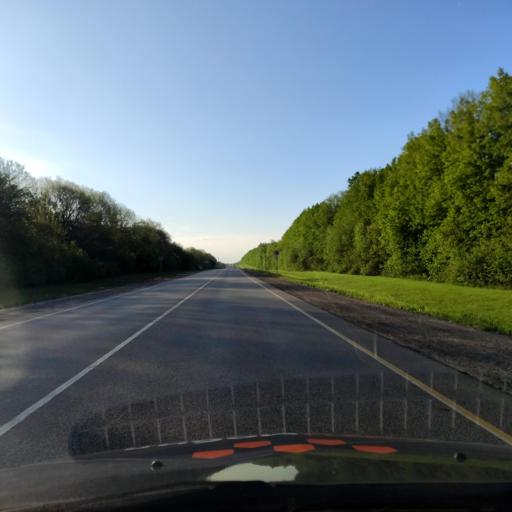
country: RU
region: Lipetsk
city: Yelets
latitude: 52.5719
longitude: 38.6579
